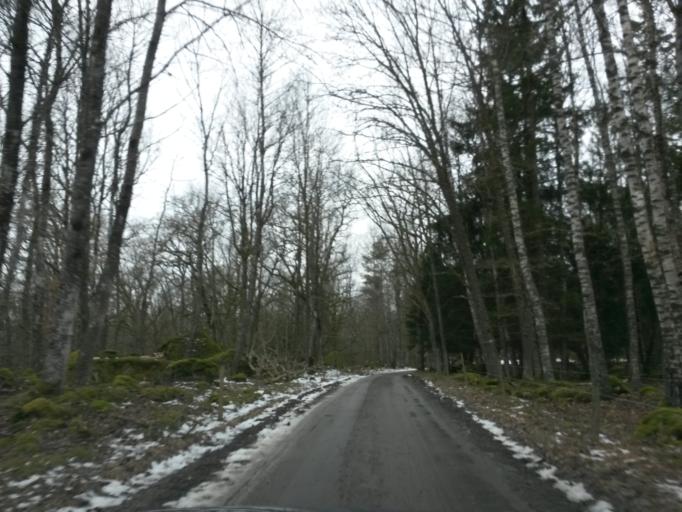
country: SE
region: Vaestra Goetaland
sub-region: Vargarda Kommun
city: Vargarda
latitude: 58.0351
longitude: 12.9151
